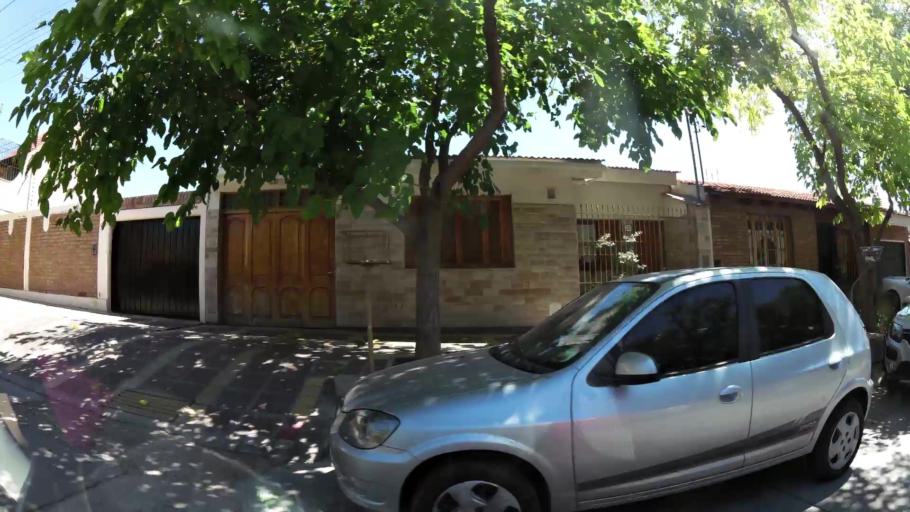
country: AR
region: Mendoza
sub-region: Departamento de Godoy Cruz
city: Godoy Cruz
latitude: -32.9472
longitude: -68.8631
